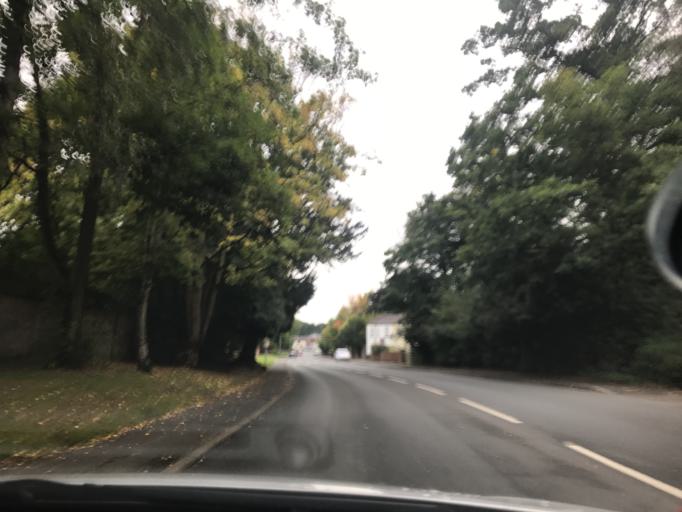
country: GB
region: England
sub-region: Cheshire West and Chester
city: Northwich
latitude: 53.2330
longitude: -2.5102
